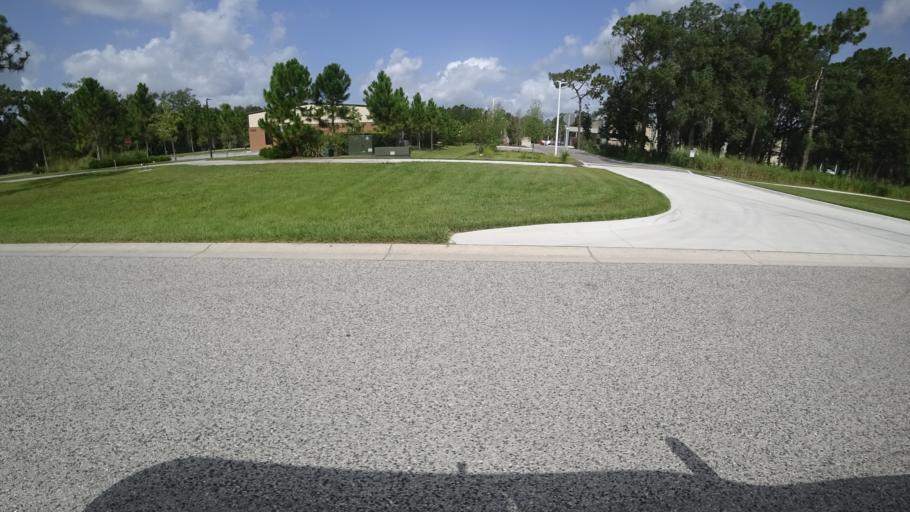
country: US
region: Florida
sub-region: Sarasota County
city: Desoto Lakes
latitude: 27.4488
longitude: -82.4559
